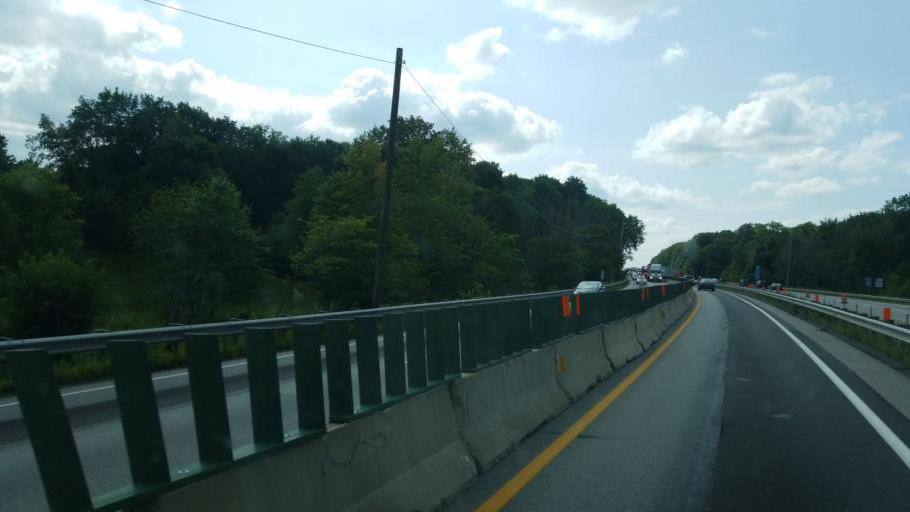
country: US
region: Ohio
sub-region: Medina County
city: Wadsworth
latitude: 41.0473
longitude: -81.6991
